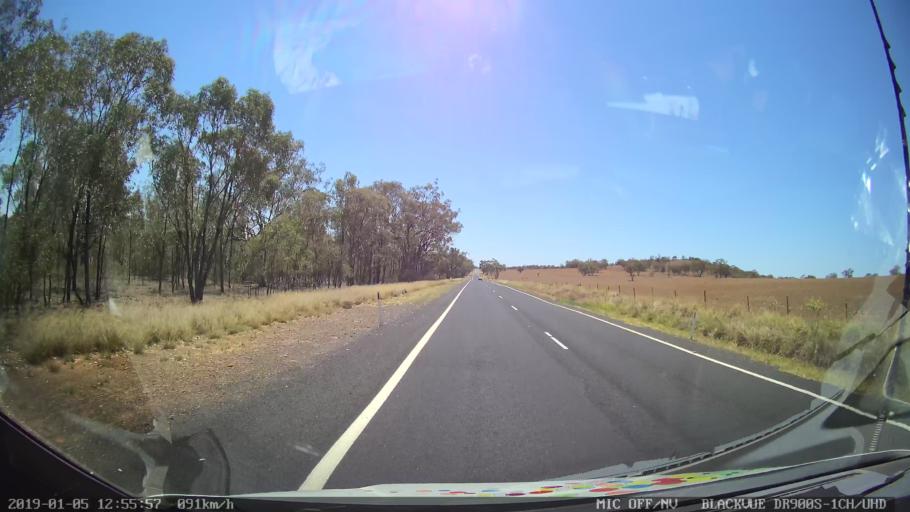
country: AU
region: New South Wales
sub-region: Warrumbungle Shire
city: Coonabarabran
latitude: -31.1180
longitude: 149.7134
